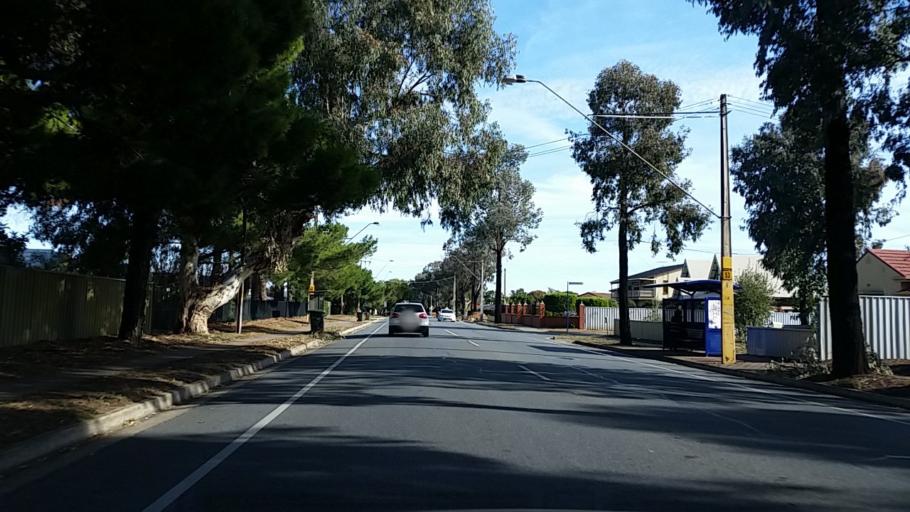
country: AU
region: South Australia
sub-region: Salisbury
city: Salisbury
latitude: -34.7633
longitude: 138.6564
